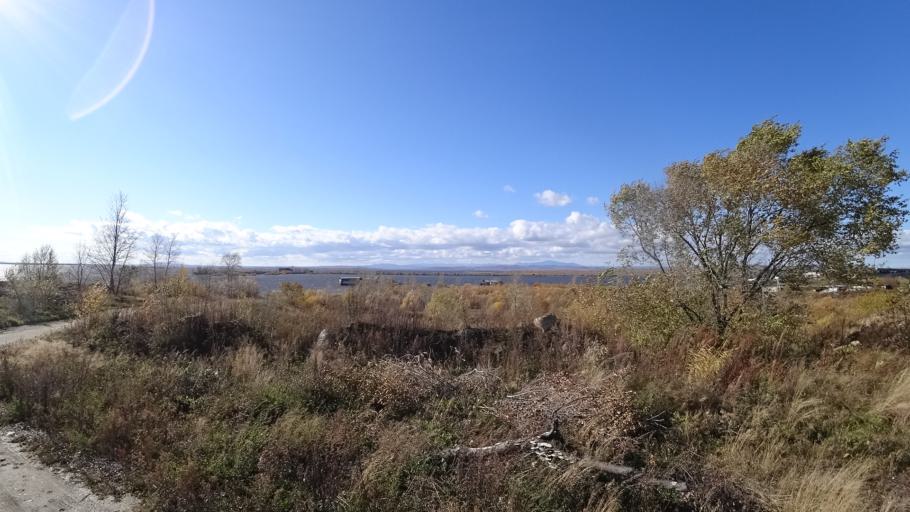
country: RU
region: Khabarovsk Krai
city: Amursk
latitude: 50.2156
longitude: 136.8889
